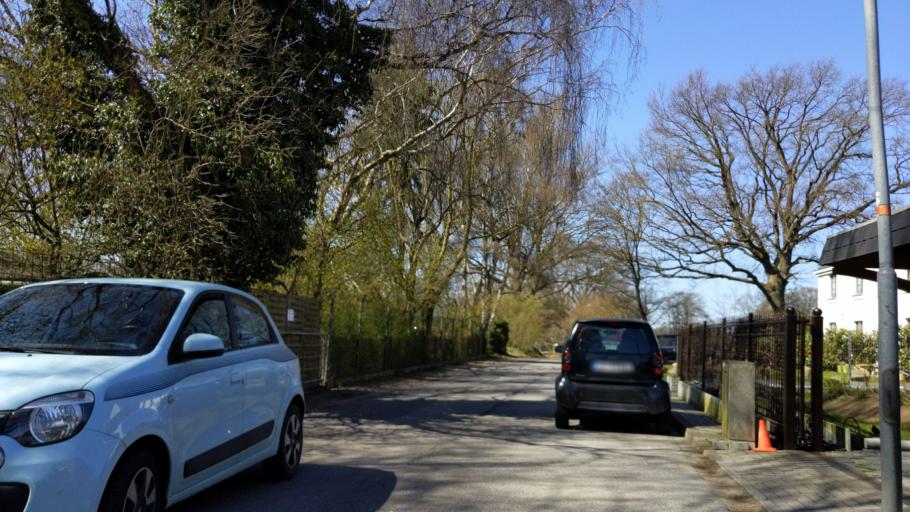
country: DE
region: Schleswig-Holstein
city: Ratekau
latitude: 53.9698
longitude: 10.6980
